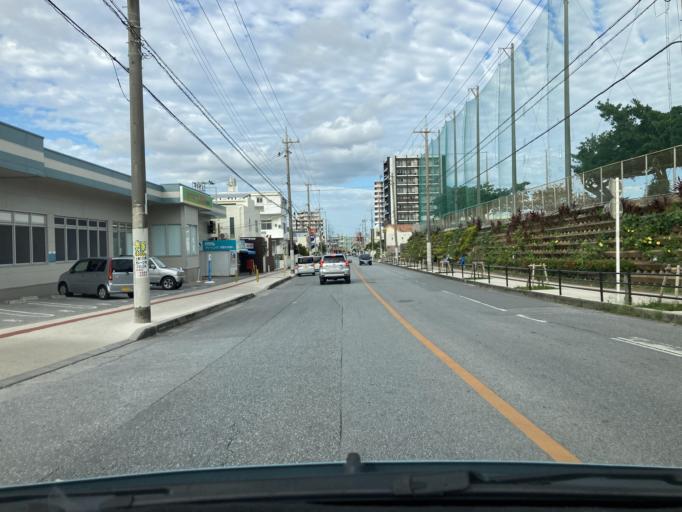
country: JP
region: Okinawa
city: Okinawa
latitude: 26.3387
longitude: 127.8212
